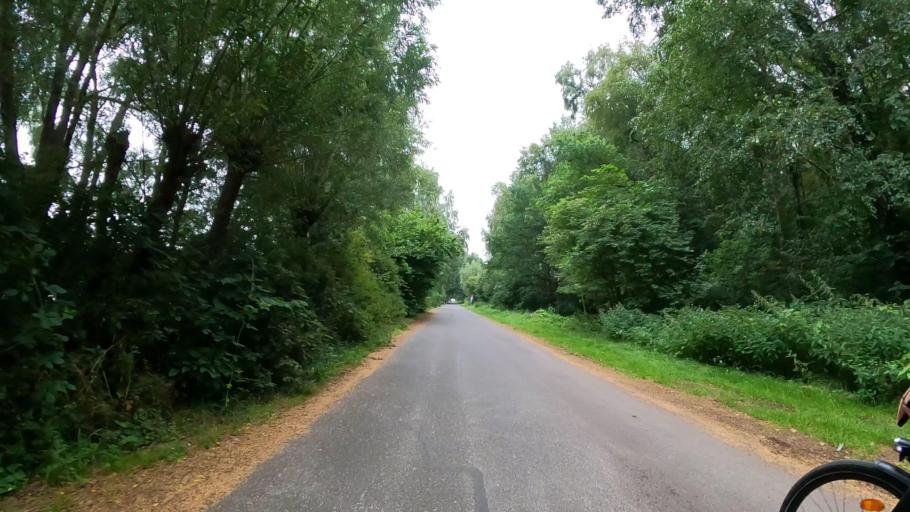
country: DE
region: Lower Saxony
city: Stelle
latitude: 53.4175
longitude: 10.0495
